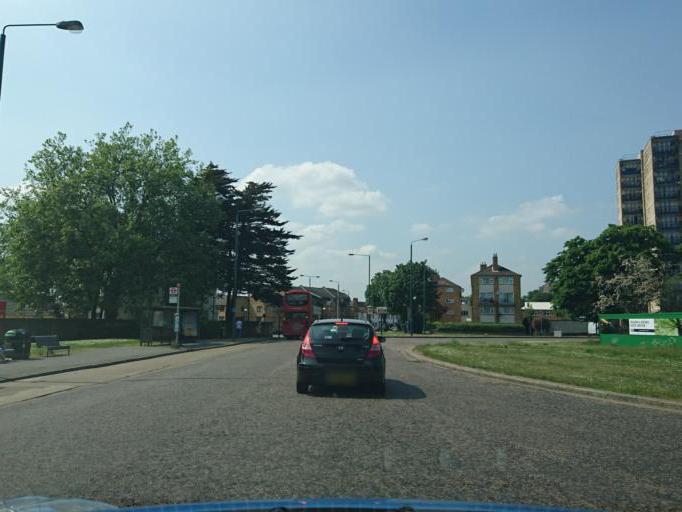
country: GB
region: England
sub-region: Greater London
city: Walthamstow
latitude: 51.5810
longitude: 0.0017
